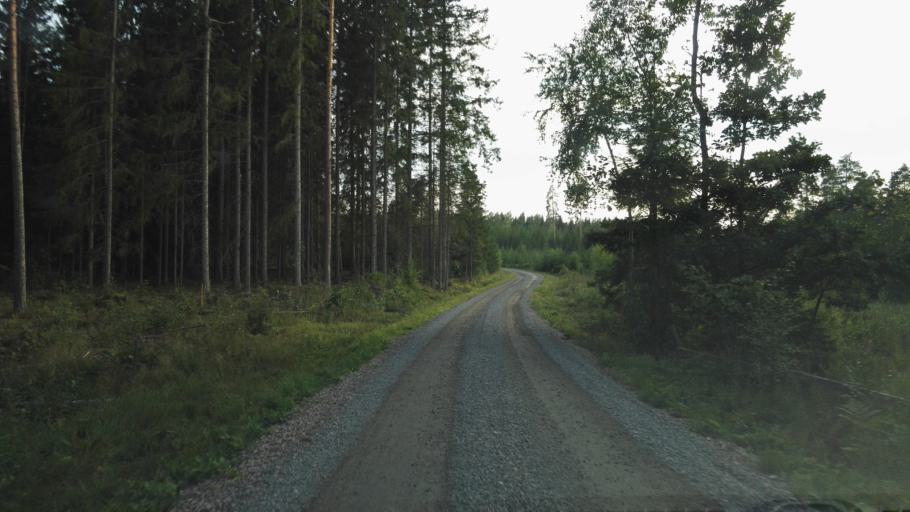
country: SE
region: Joenkoeping
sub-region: Vetlanda Kommun
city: Landsbro
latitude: 57.2552
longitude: 14.8918
